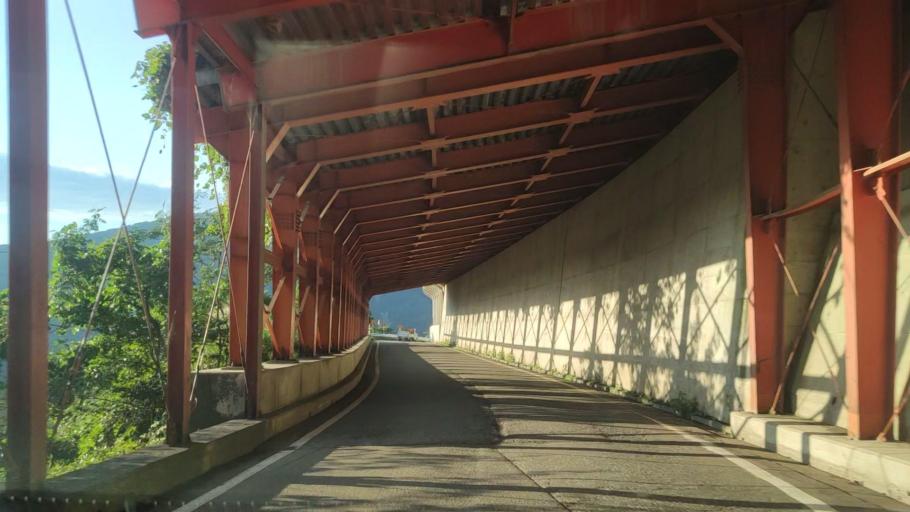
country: JP
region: Toyama
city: Yatsuomachi-higashikumisaka
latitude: 36.5059
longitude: 137.0224
